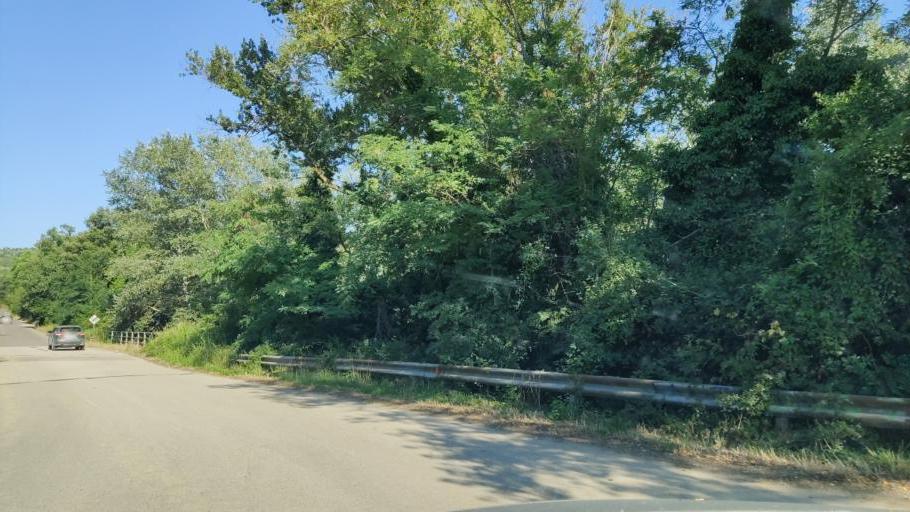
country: IT
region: Umbria
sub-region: Provincia di Terni
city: Penna in Teverina
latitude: 42.4789
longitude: 12.3640
